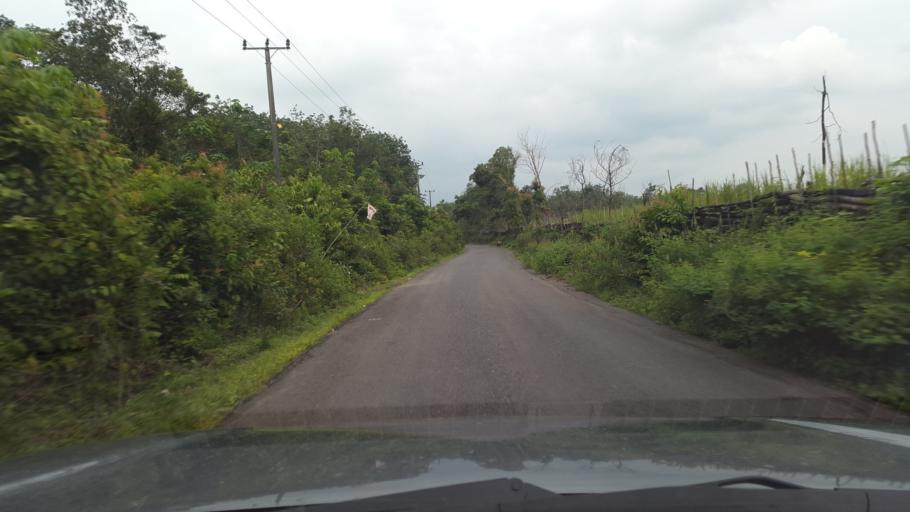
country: ID
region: South Sumatra
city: Gunungmenang
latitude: -3.0989
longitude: 103.8889
